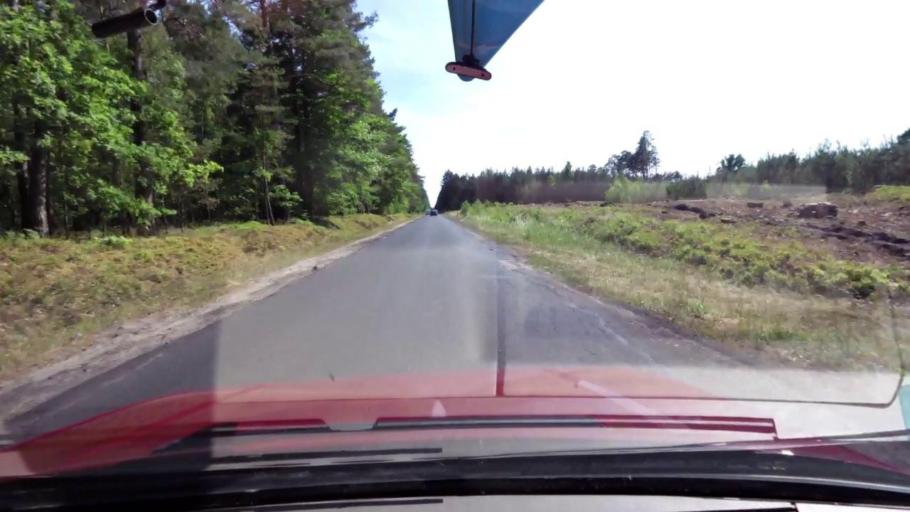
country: PL
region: Pomeranian Voivodeship
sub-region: Powiat slupski
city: Kepice
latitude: 54.3085
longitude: 16.9624
